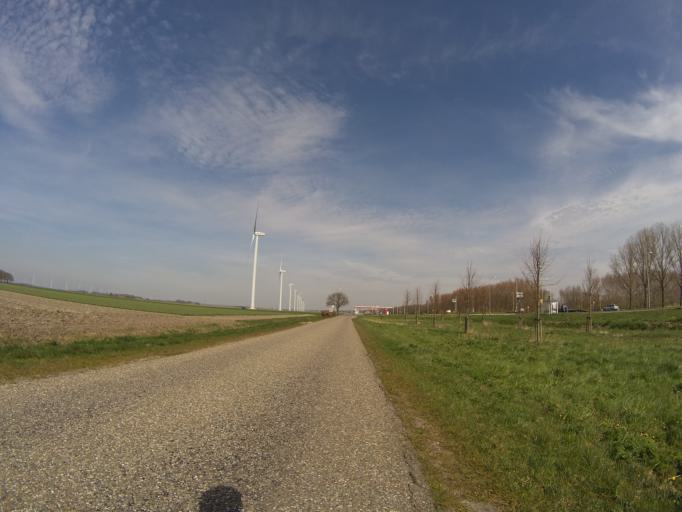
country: NL
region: Gelderland
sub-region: Gemeente Nijkerk
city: Nijkerk
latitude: 52.2801
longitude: 5.4618
